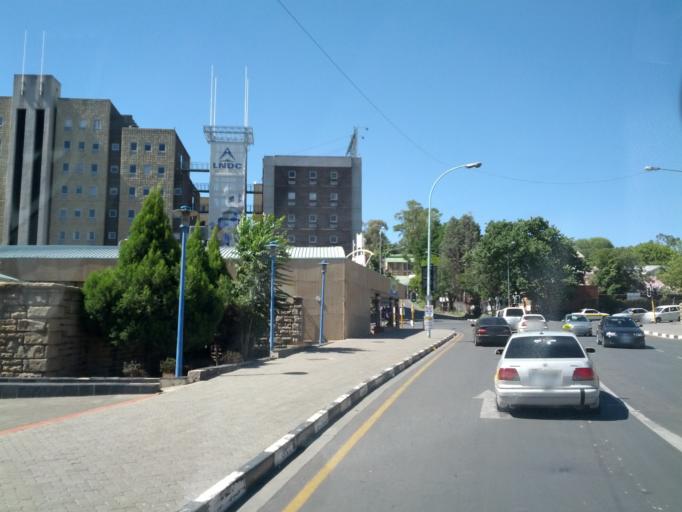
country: LS
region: Maseru
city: Maseru
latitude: -29.3141
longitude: 27.4802
